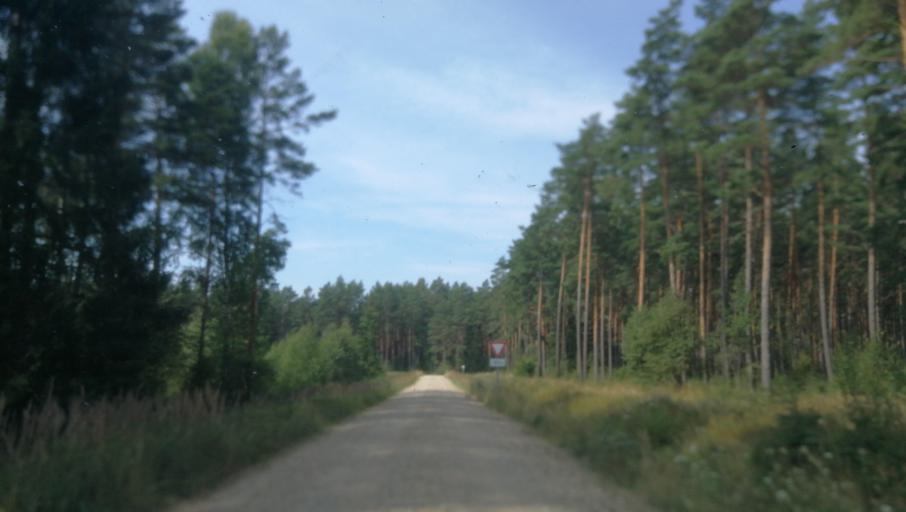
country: LV
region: Pavilostas
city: Pavilosta
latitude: 56.8198
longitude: 21.2930
